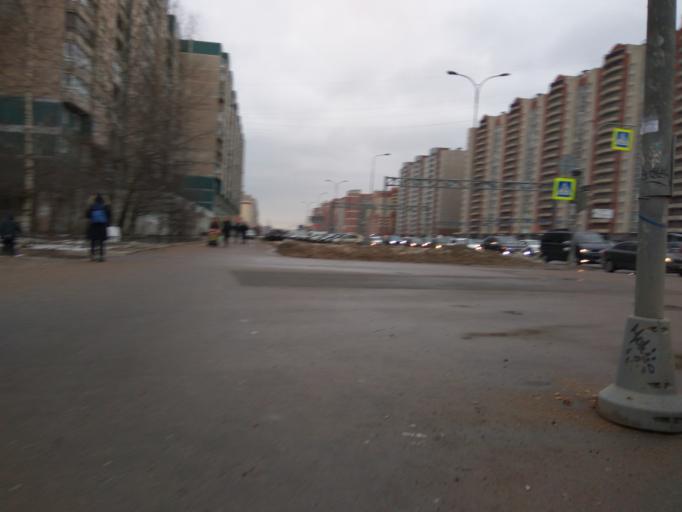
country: RU
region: St.-Petersburg
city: Staraya Derevnya
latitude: 60.0043
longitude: 30.2354
